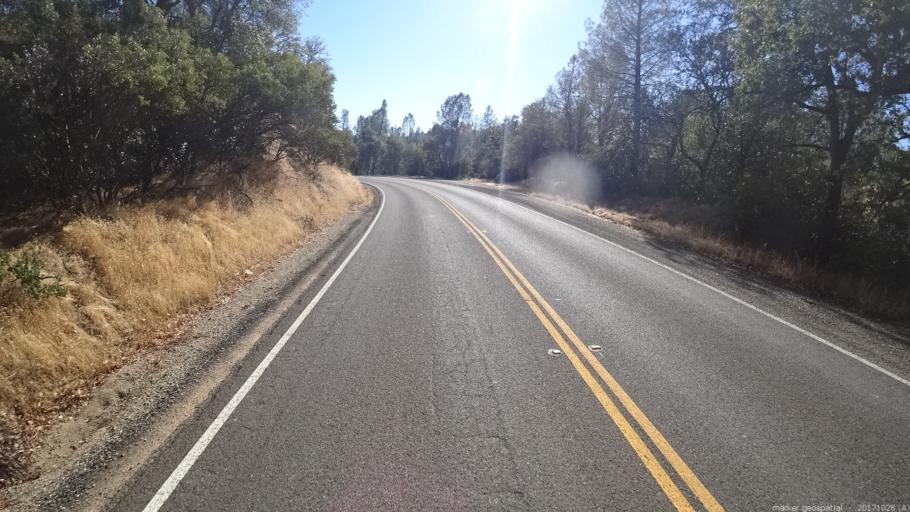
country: US
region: California
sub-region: Shasta County
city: Shasta
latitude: 40.6011
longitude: -122.4651
